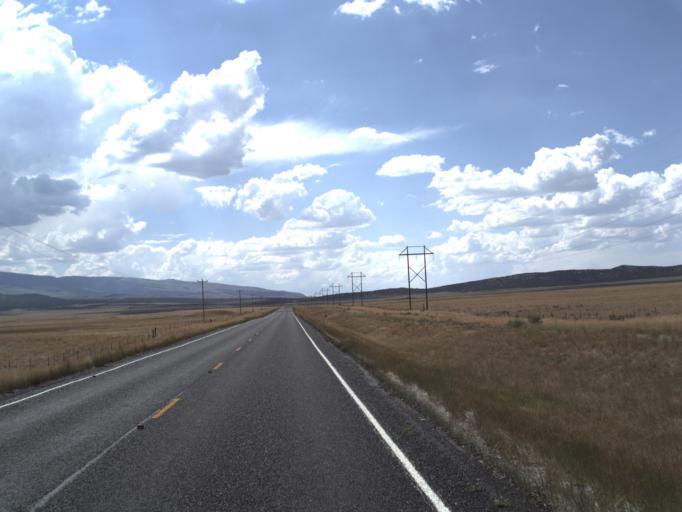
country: US
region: Idaho
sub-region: Power County
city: American Falls
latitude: 41.9676
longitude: -113.0876
